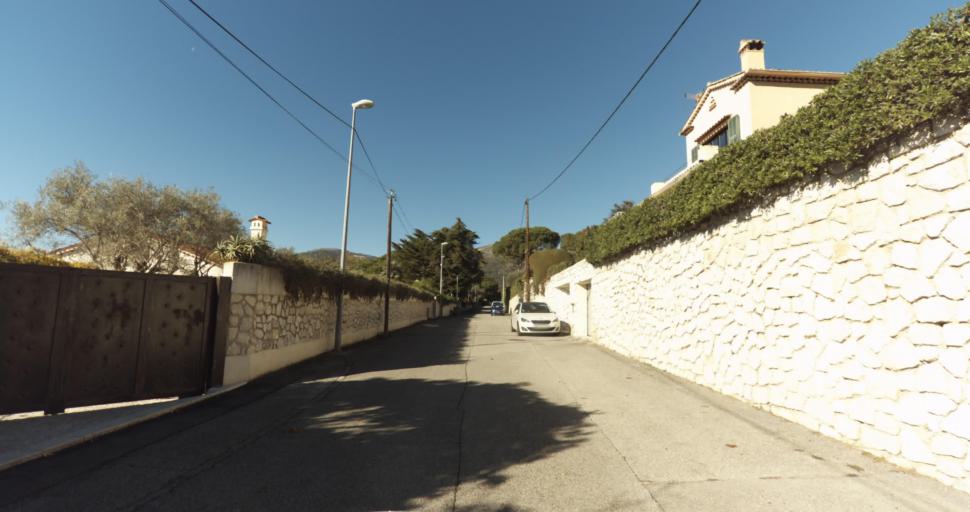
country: FR
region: Provence-Alpes-Cote d'Azur
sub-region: Departement des Alpes-Maritimes
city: Vence
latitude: 43.7172
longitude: 7.1104
